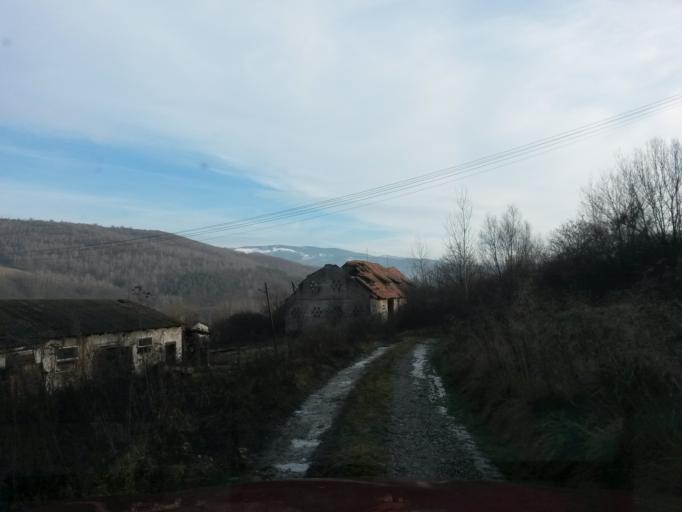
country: SK
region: Kosicky
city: Roznava
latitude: 48.7101
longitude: 20.4406
